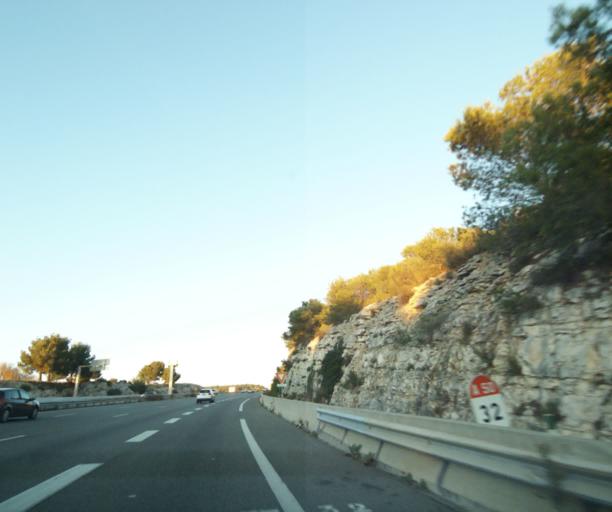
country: FR
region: Provence-Alpes-Cote d'Azur
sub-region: Departement des Bouches-du-Rhone
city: Roquefort-la-Bedoule
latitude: 43.2276
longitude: 5.5833
